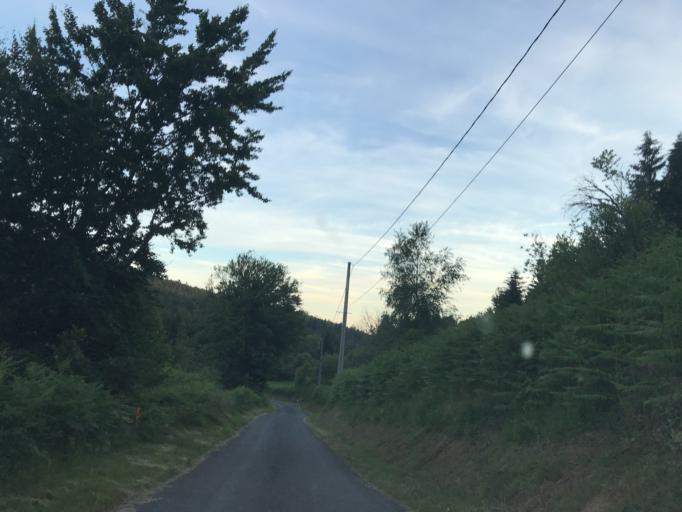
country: FR
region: Rhone-Alpes
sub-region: Departement de la Loire
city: Noiretable
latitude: 45.8007
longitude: 3.7037
